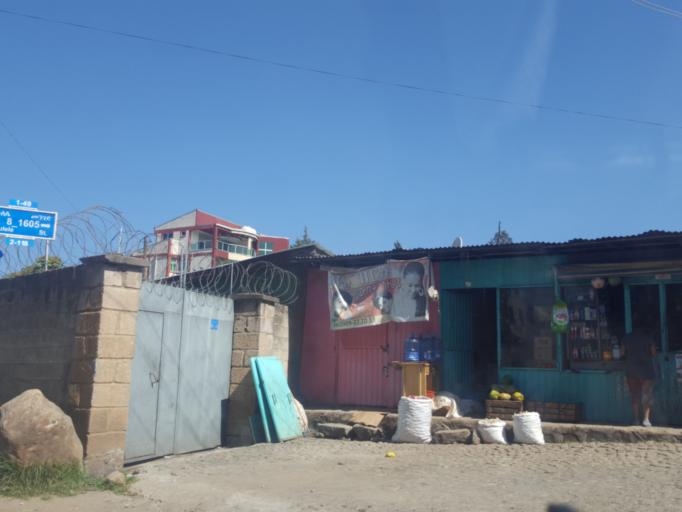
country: ET
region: Adis Abeba
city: Addis Ababa
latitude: 9.0540
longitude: 38.7403
